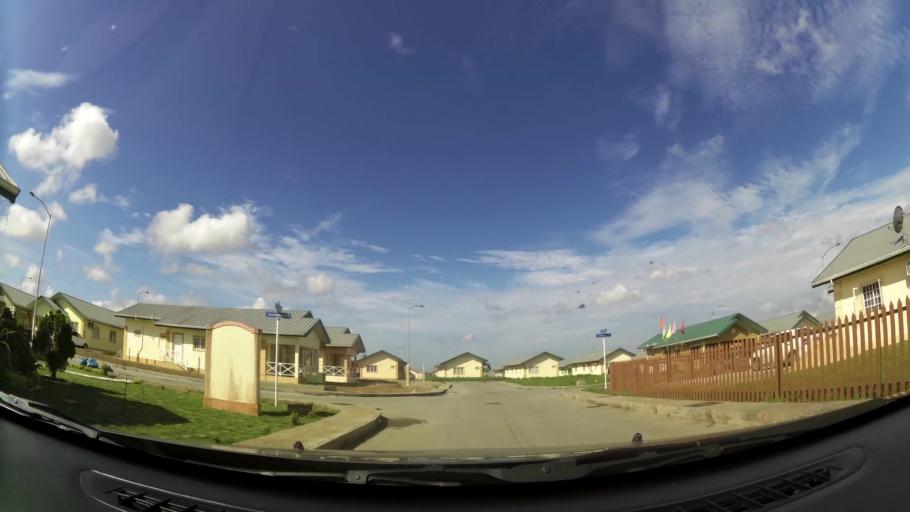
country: TT
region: Chaguanas
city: Chaguanas
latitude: 10.5347
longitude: -61.3938
